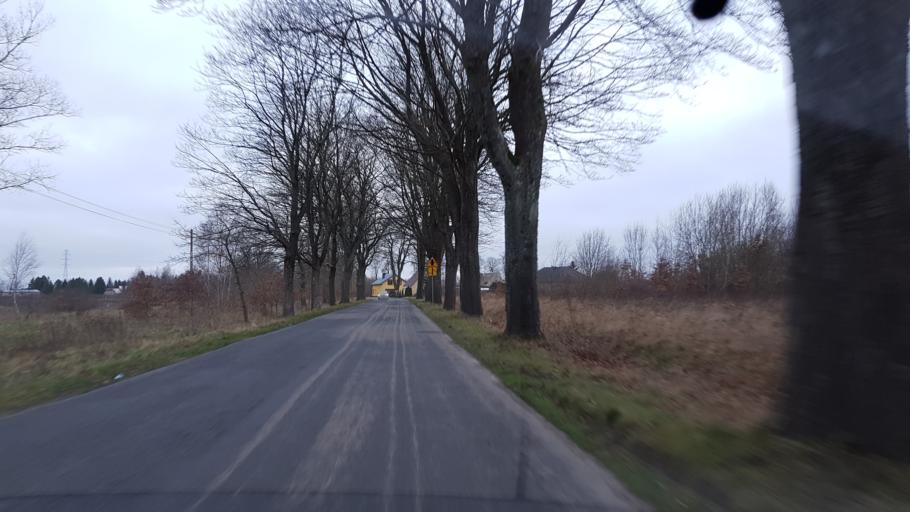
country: PL
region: West Pomeranian Voivodeship
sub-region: Powiat slawienski
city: Slawno
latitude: 54.3649
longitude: 16.7456
